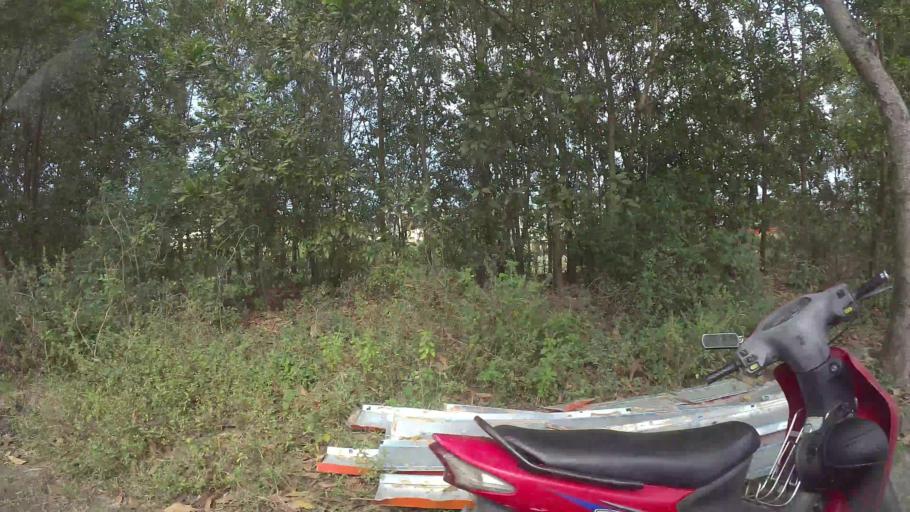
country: VN
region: Da Nang
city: Lien Chieu
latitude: 16.0566
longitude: 108.1610
